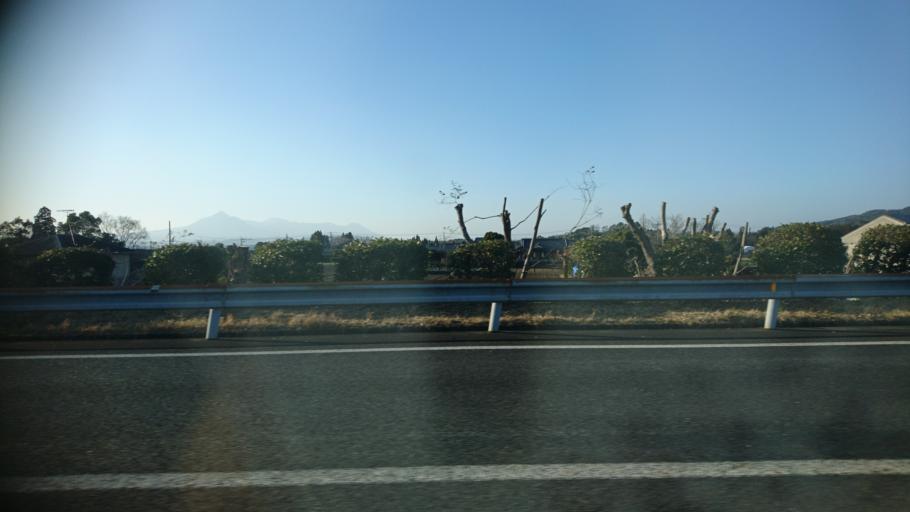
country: JP
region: Miyazaki
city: Miyakonojo
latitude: 31.7886
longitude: 131.1509
